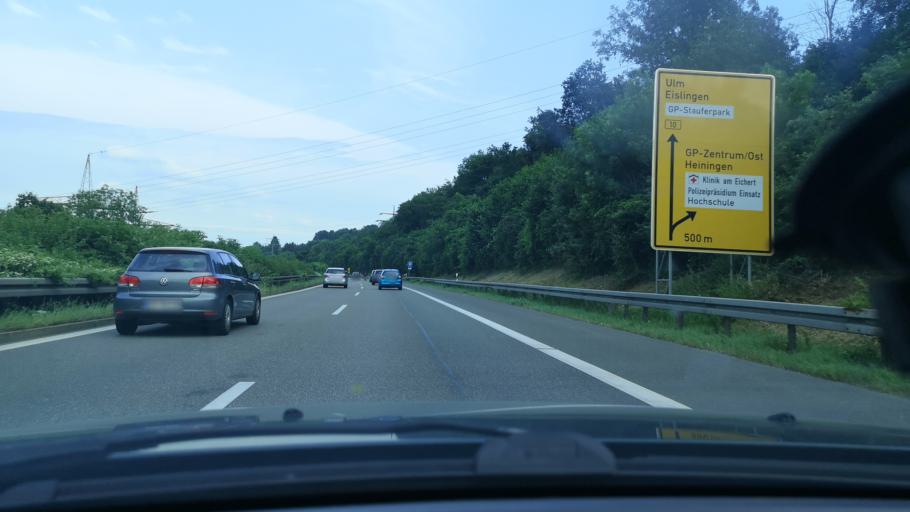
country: DE
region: Baden-Wuerttemberg
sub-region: Regierungsbezirk Stuttgart
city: Goeppingen
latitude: 48.6944
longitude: 9.6579
